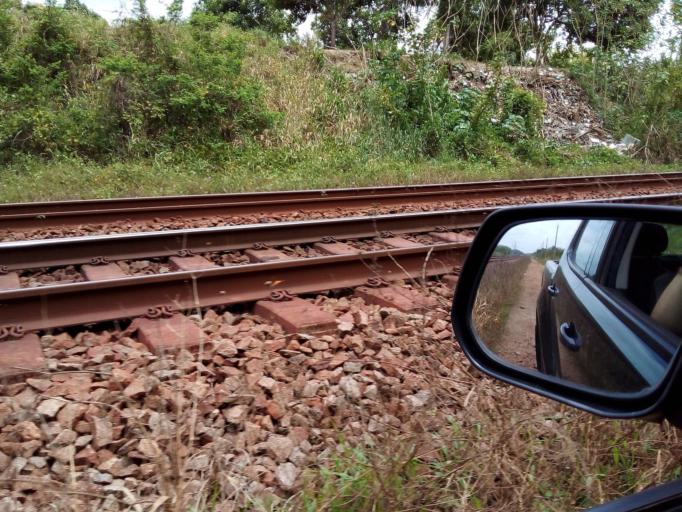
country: BR
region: Maranhao
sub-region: Sao Luis
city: Sao Luis
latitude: -2.6985
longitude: -44.3088
